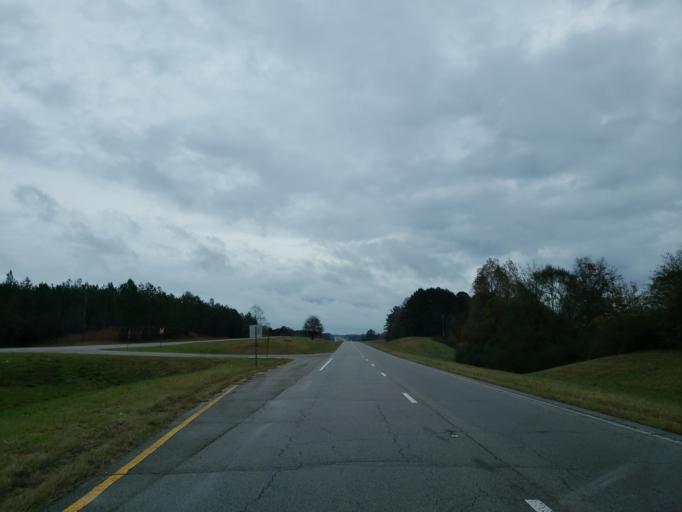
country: US
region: Mississippi
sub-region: Wayne County
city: Waynesboro
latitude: 31.6966
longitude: -88.8681
